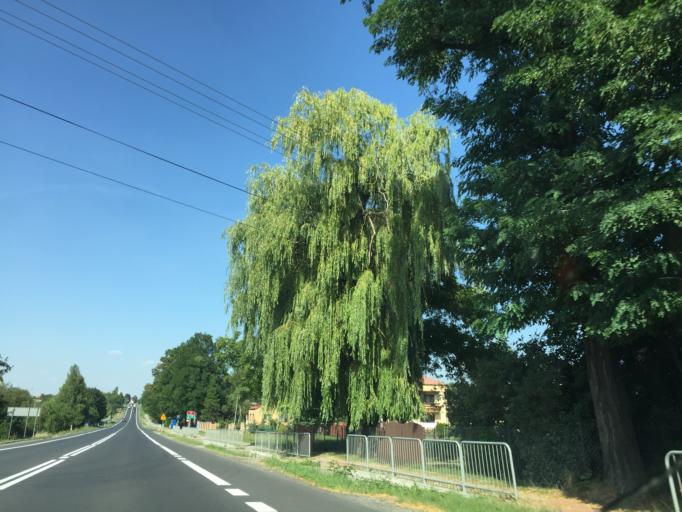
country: PL
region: Lesser Poland Voivodeship
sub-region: Powiat krakowski
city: Michalowice
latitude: 50.1930
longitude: 20.0051
